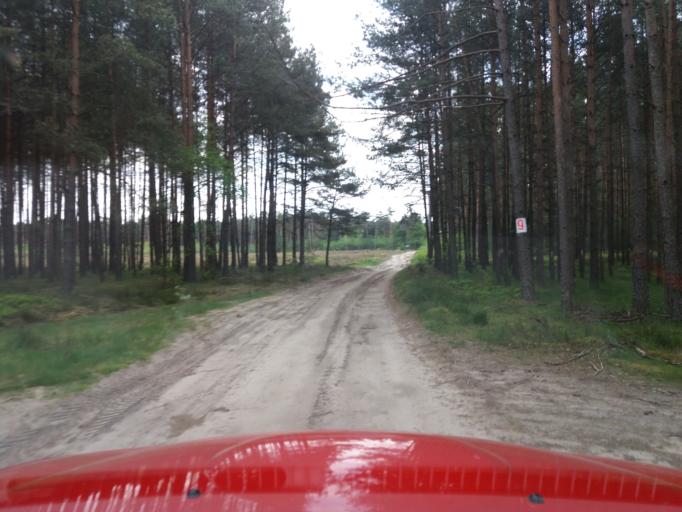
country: PL
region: West Pomeranian Voivodeship
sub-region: Powiat choszczenski
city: Drawno
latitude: 53.1342
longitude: 15.7653
